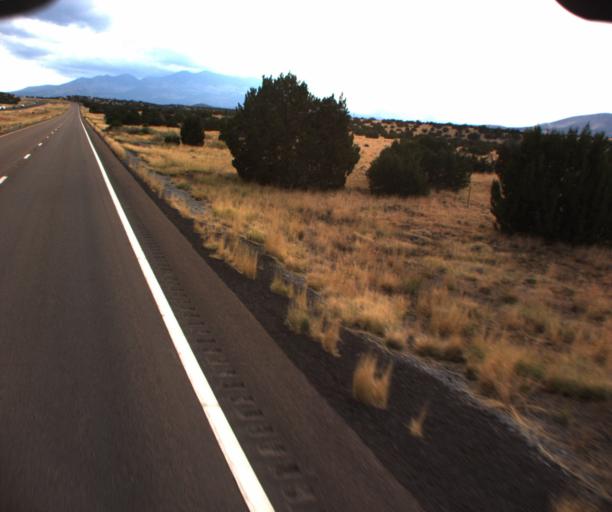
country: US
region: Arizona
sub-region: Coconino County
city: Flagstaff
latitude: 35.4999
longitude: -111.5517
